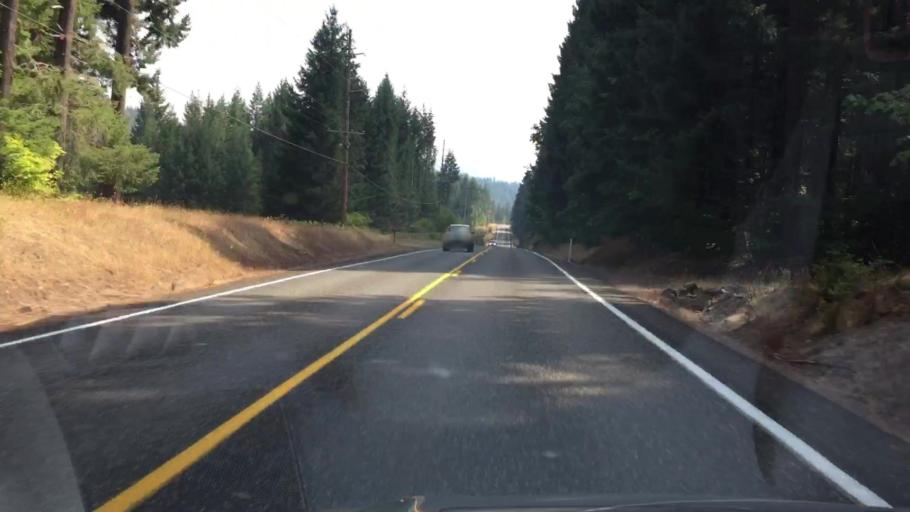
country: US
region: Washington
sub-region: Klickitat County
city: White Salmon
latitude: 45.8747
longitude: -121.5181
